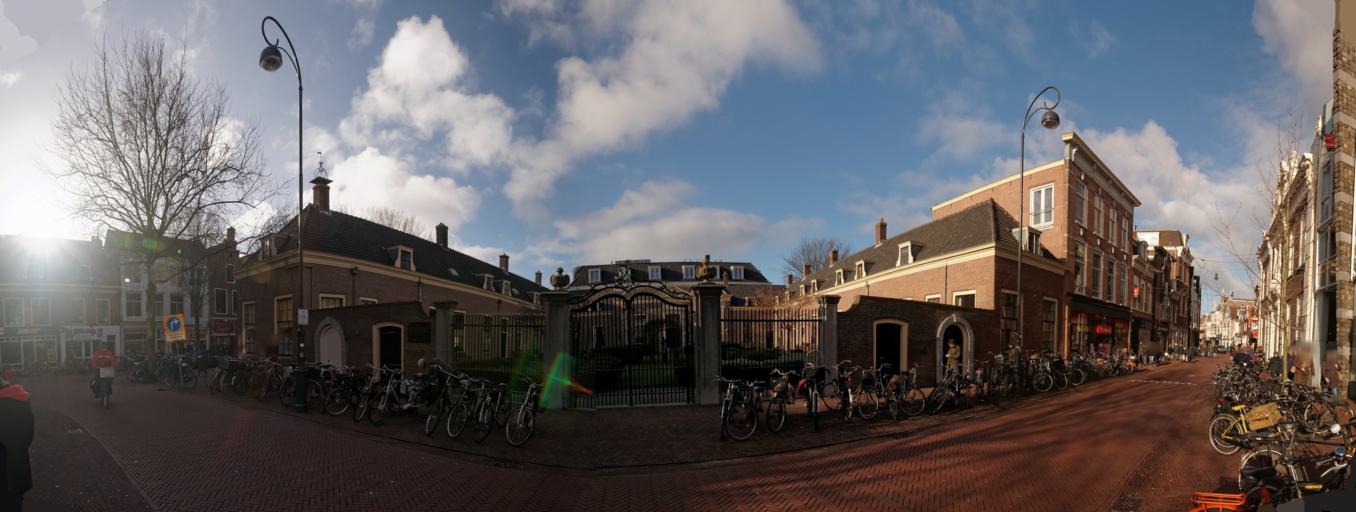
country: NL
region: North Holland
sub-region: Gemeente Haarlem
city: Haarlem
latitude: 52.3831
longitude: 4.6353
